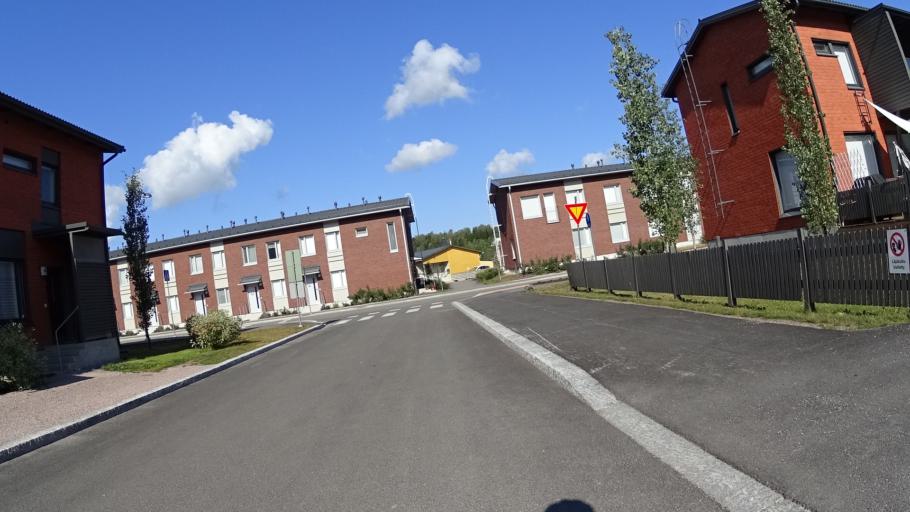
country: FI
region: Uusimaa
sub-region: Helsinki
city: Espoo
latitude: 60.1902
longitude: 24.5889
